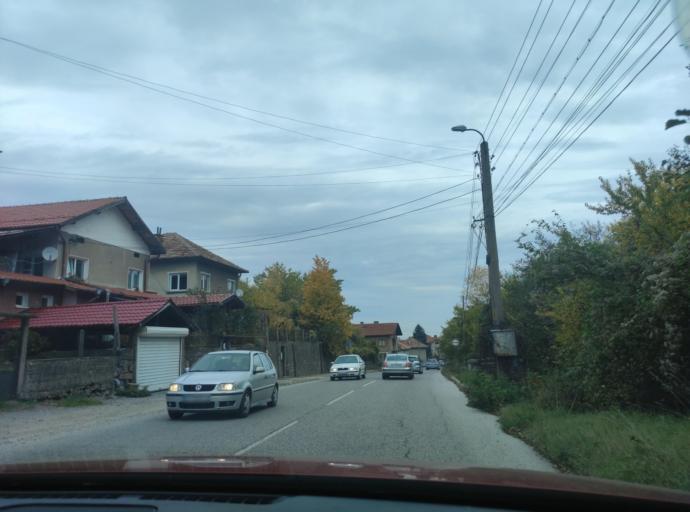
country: BG
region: Montana
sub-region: Obshtina Berkovitsa
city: Berkovitsa
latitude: 43.1932
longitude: 23.1602
